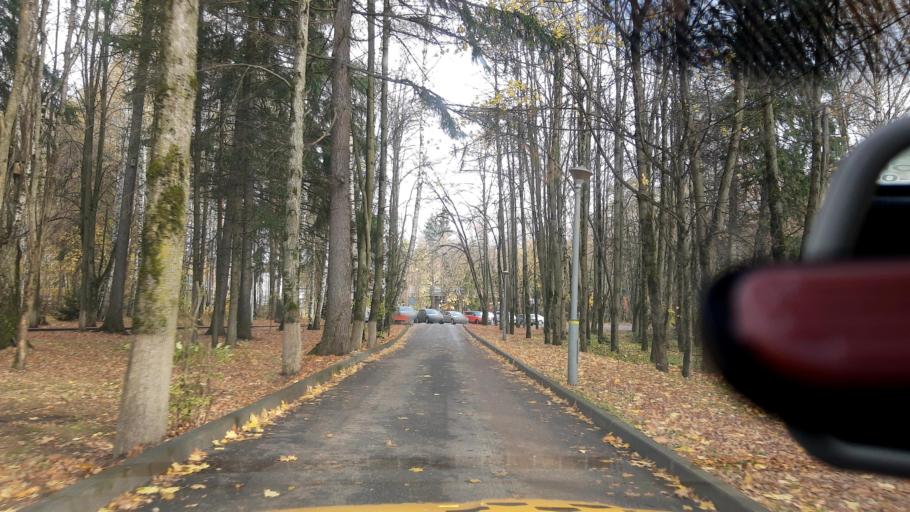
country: RU
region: Moskovskaya
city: Golitsyno
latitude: 55.6164
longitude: 37.0010
